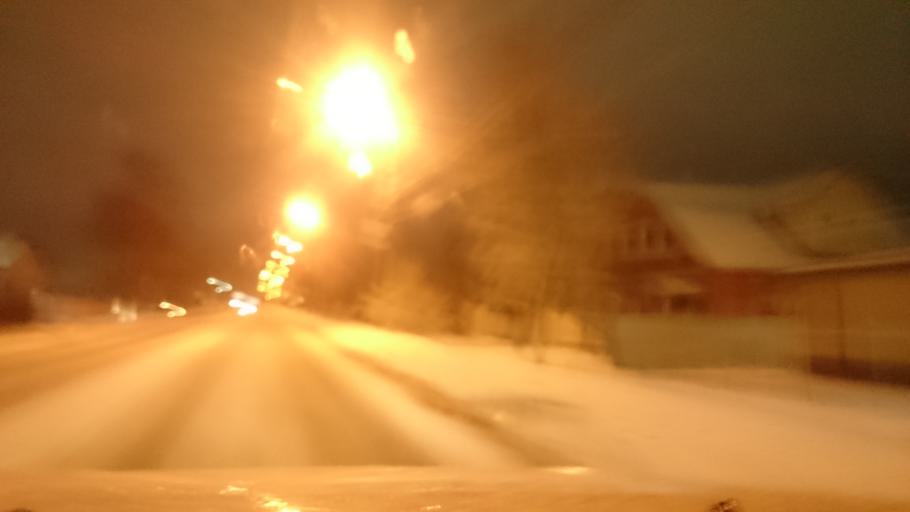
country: RU
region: Tula
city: Tula
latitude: 54.1952
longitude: 37.5532
